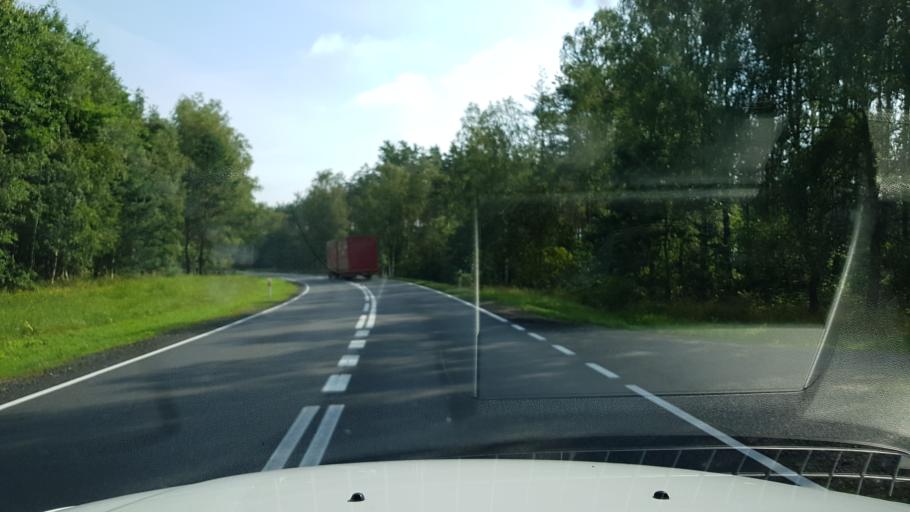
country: PL
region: West Pomeranian Voivodeship
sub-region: Powiat walecki
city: Miroslawiec
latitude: 53.3338
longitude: 16.0625
